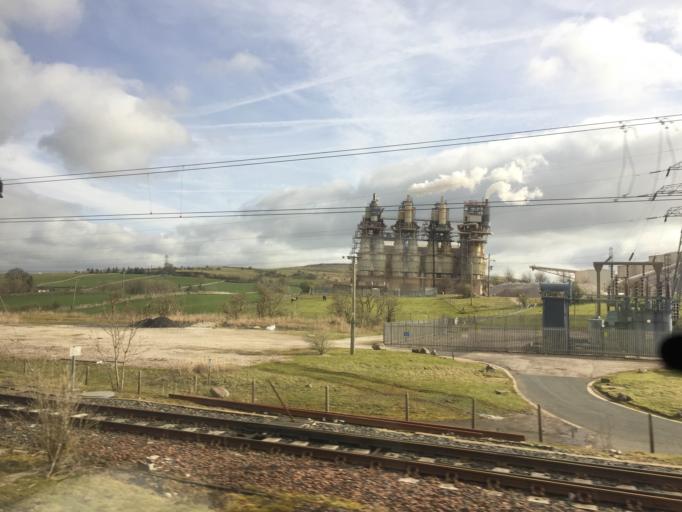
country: GB
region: England
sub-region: Cumbria
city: Penrith
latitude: 54.5138
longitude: -2.6685
